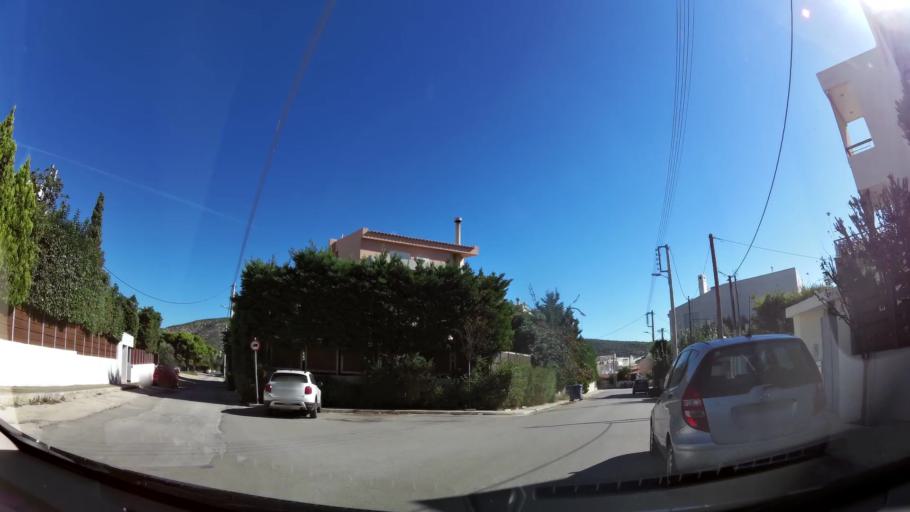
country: GR
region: Attica
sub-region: Nomarchia Anatolikis Attikis
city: Vari
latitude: 37.8378
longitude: 23.8157
